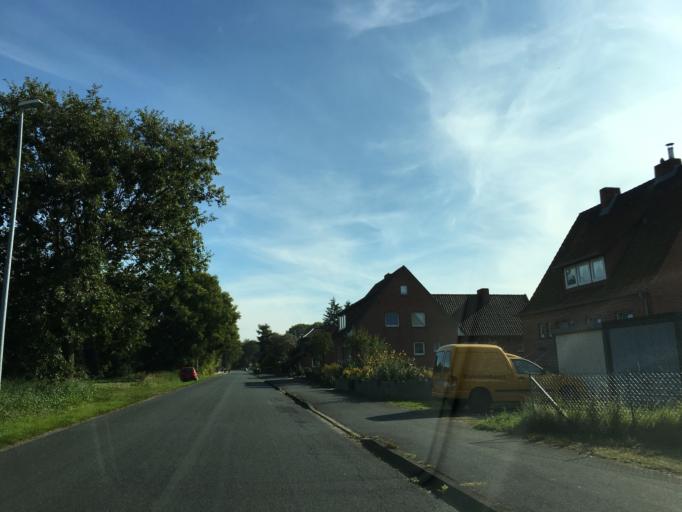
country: DE
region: Lower Saxony
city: Adendorf
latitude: 53.2773
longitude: 10.4696
